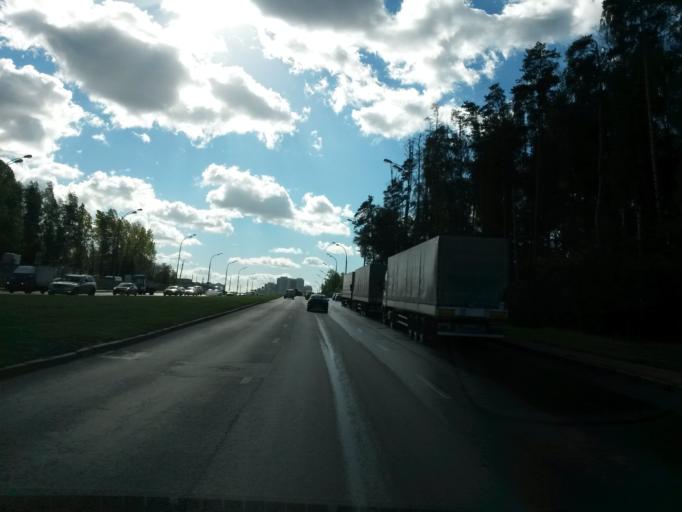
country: RU
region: Moscow
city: Chertanovo Yuzhnoye
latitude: 55.5614
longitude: 37.5552
